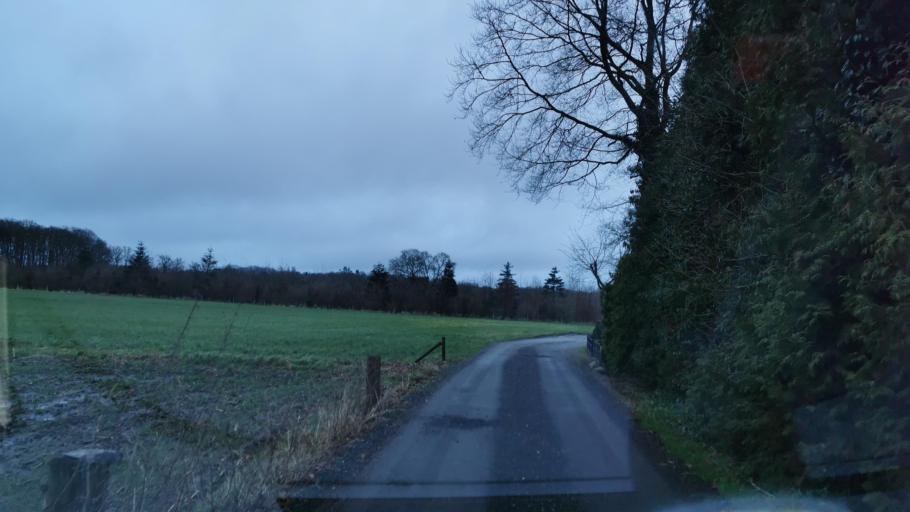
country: NL
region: Overijssel
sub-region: Gemeente Oldenzaal
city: Oldenzaal
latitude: 52.3163
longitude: 6.9694
